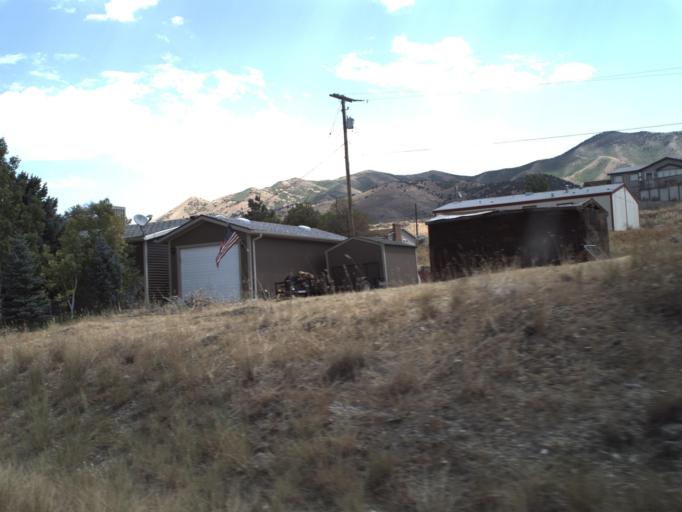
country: US
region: Utah
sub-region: Tooele County
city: Tooele
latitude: 40.4455
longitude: -112.3653
